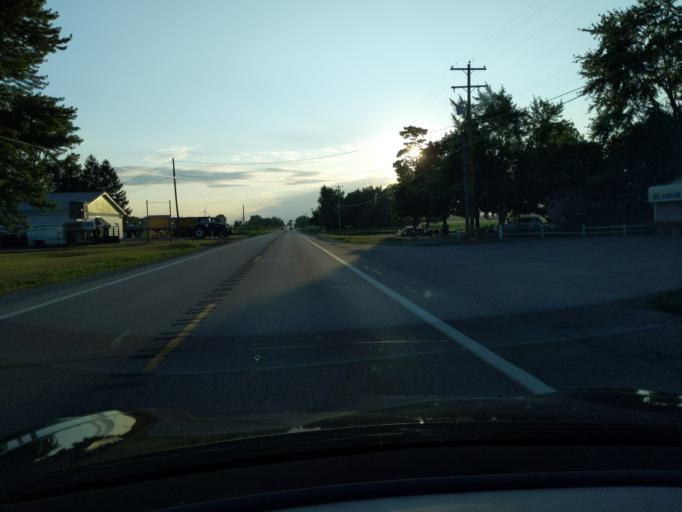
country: US
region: Michigan
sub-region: Gratiot County
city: Breckenridge
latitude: 43.4080
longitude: -84.4918
